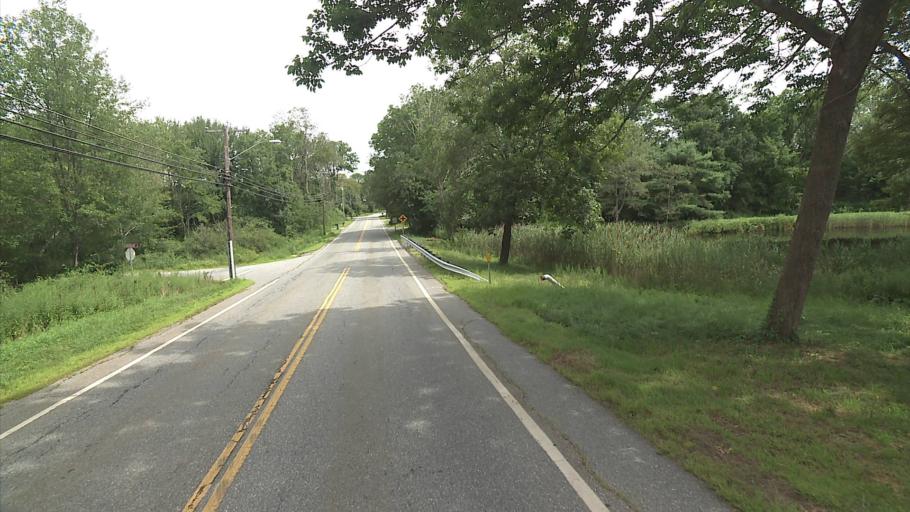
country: US
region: Connecticut
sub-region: Windham County
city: Thompson
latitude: 41.9622
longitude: -71.8603
